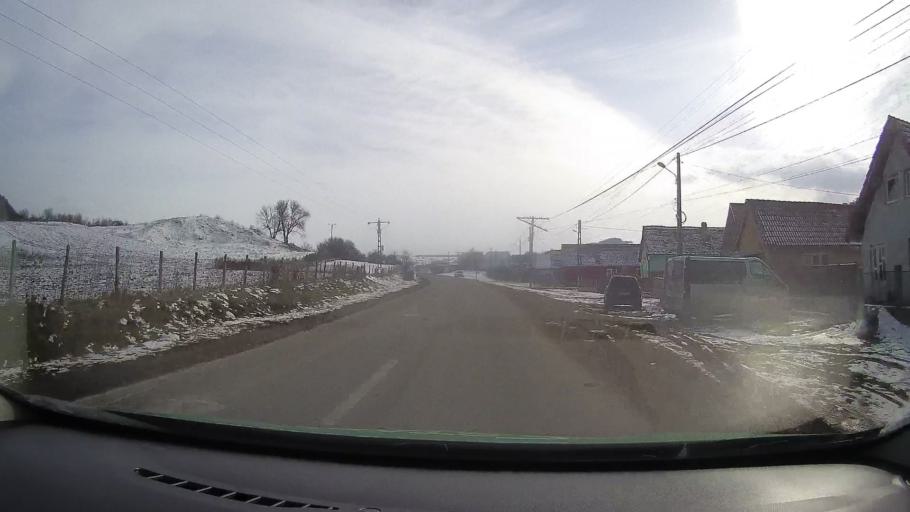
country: RO
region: Mures
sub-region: Comuna Apold
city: Apold
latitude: 46.1331
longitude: 24.8195
